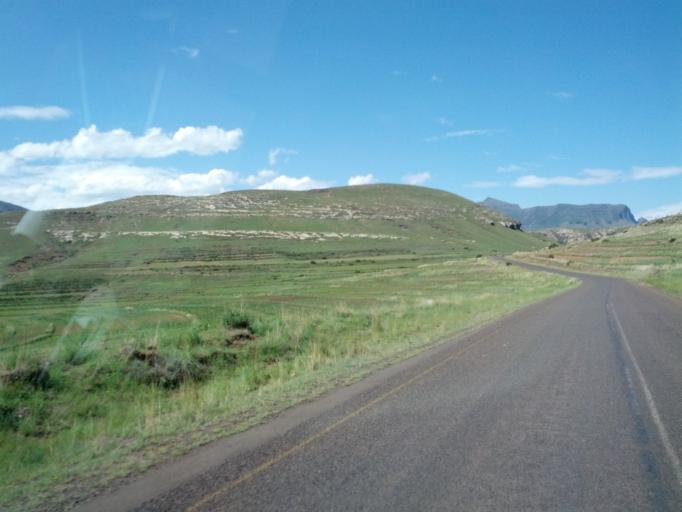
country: LS
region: Qacha's Nek
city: Qacha's Nek
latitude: -30.0531
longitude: 28.4883
